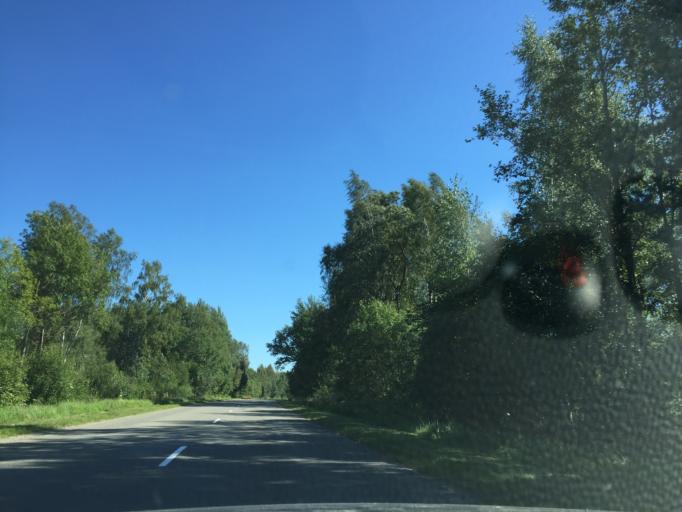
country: LV
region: Akniste
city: Akniste
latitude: 56.1401
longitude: 25.8124
